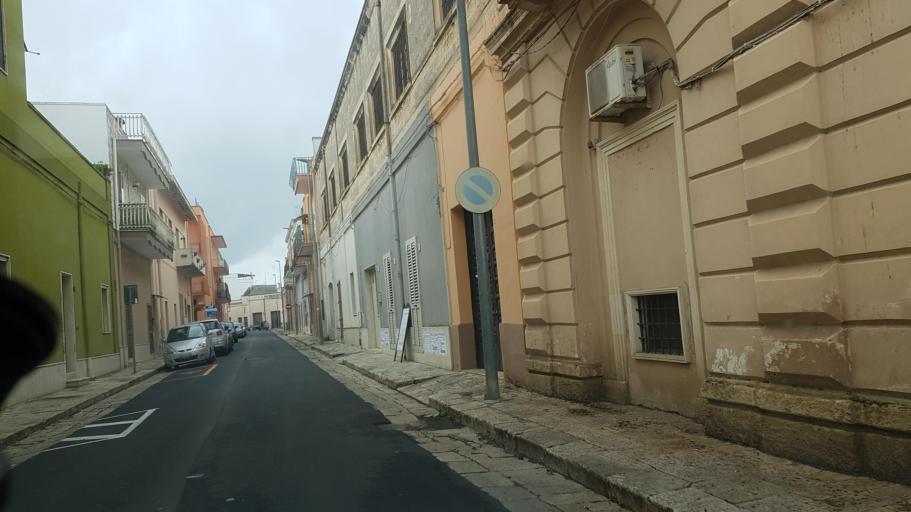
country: IT
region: Apulia
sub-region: Provincia di Lecce
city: Novoli
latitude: 40.3791
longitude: 18.0472
